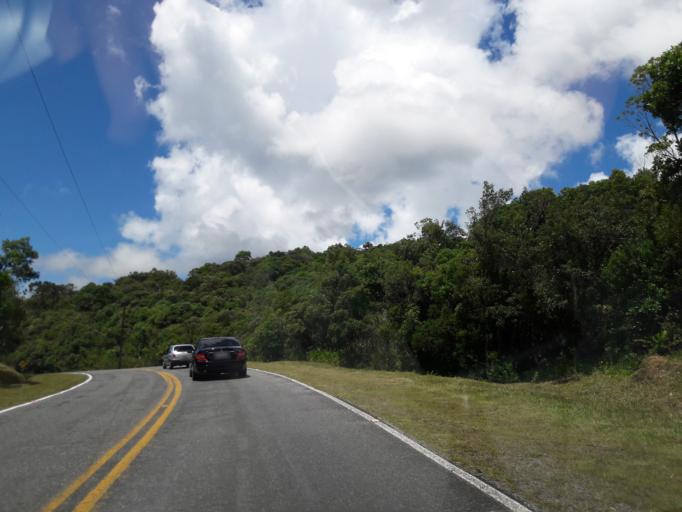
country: BR
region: Parana
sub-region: Campina Grande Do Sul
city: Campina Grande do Sul
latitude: -25.3243
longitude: -48.9211
